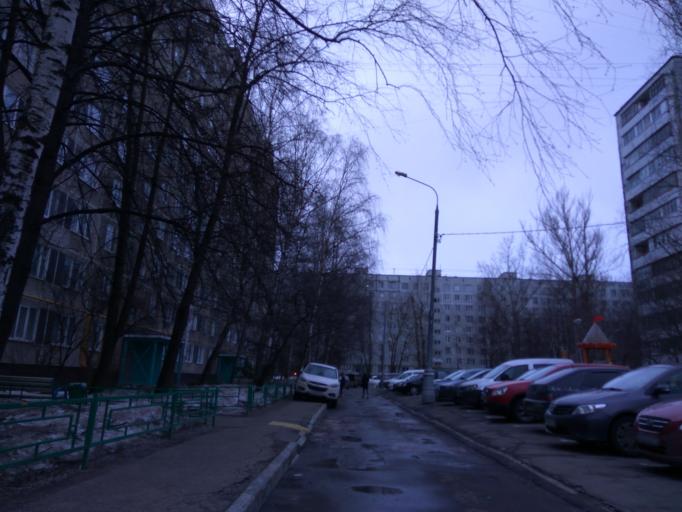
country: RU
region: Moscow
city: Biryulevo
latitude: 55.5955
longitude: 37.6654
